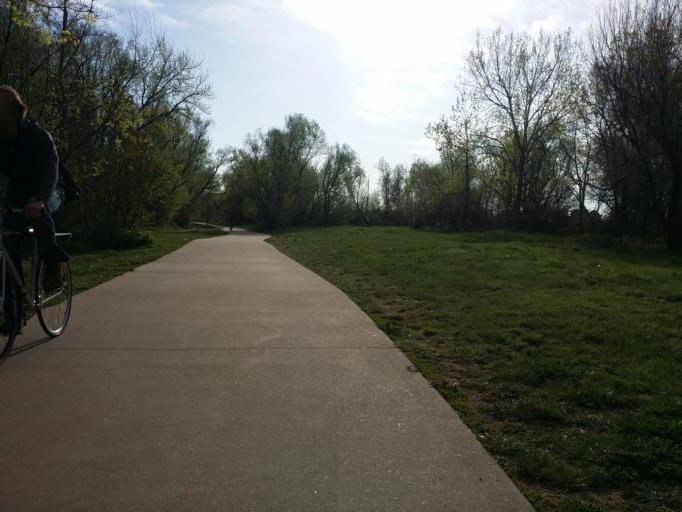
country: US
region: Colorado
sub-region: Boulder County
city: Boulder
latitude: 40.0111
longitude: -105.2508
